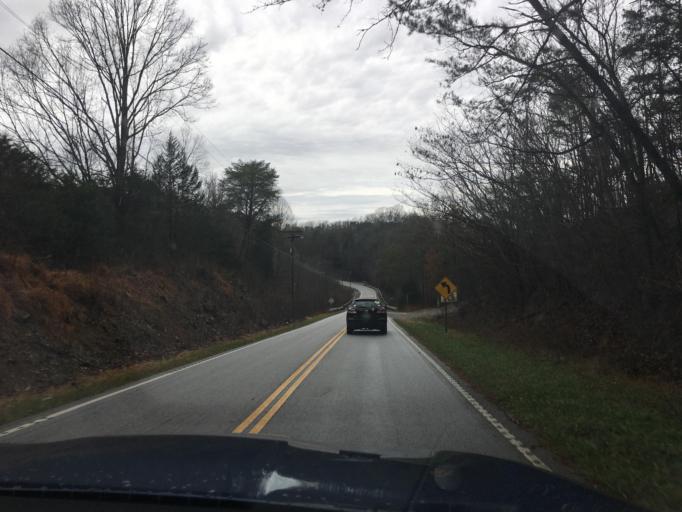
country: US
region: Tennessee
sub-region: McMinn County
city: Englewood
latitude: 35.3412
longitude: -84.3744
